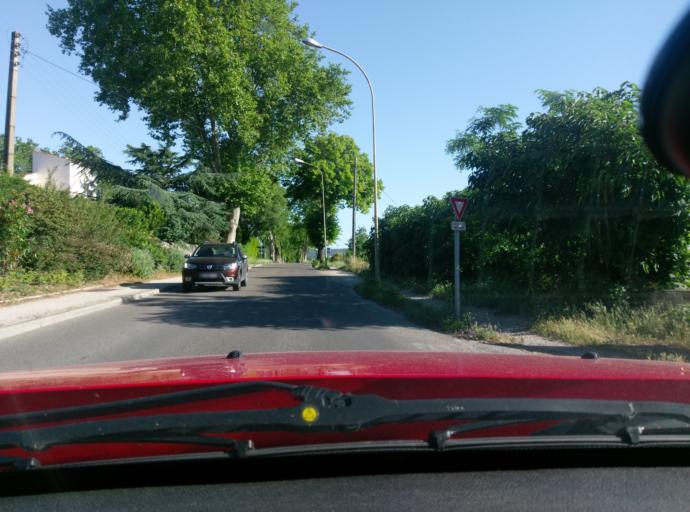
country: FR
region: Languedoc-Roussillon
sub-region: Departement du Gard
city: Uzes
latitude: 44.0205
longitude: 4.4152
